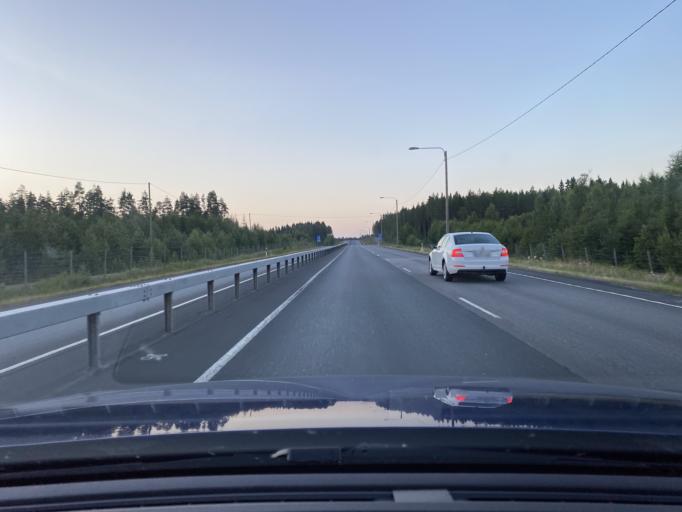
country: FI
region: Pirkanmaa
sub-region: Luoteis-Pirkanmaa
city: Parkano
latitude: 61.8855
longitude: 22.9742
